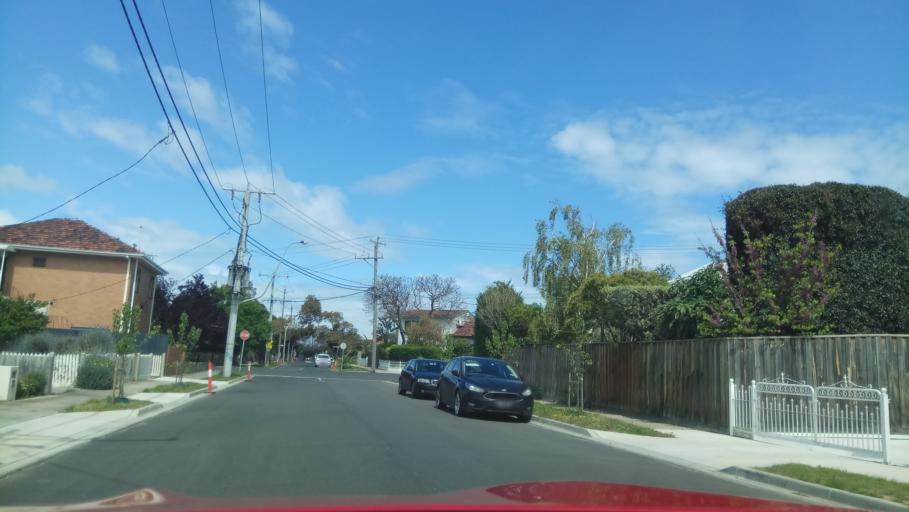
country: AU
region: Victoria
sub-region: Hobsons Bay
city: Williamstown
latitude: -37.8502
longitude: 144.8917
